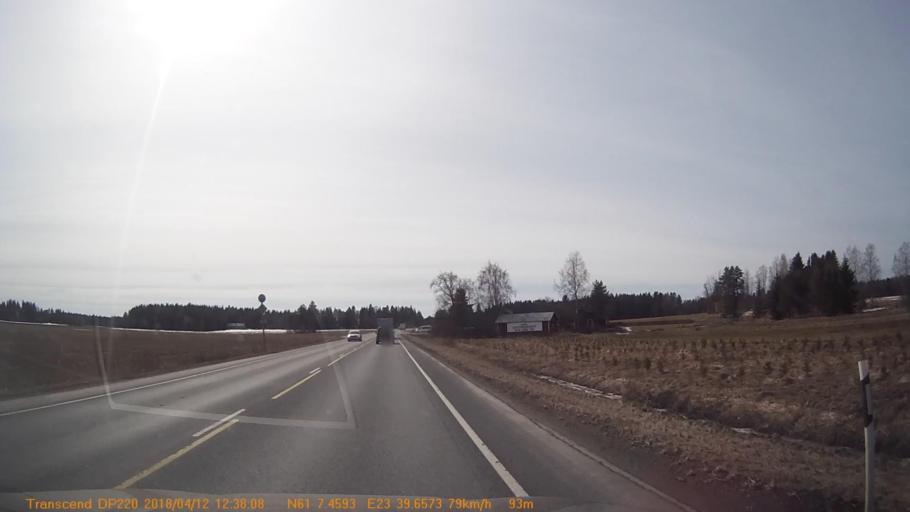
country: FI
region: Pirkanmaa
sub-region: Etelae-Pirkanmaa
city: Kylmaekoski
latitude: 61.1245
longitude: 23.6607
